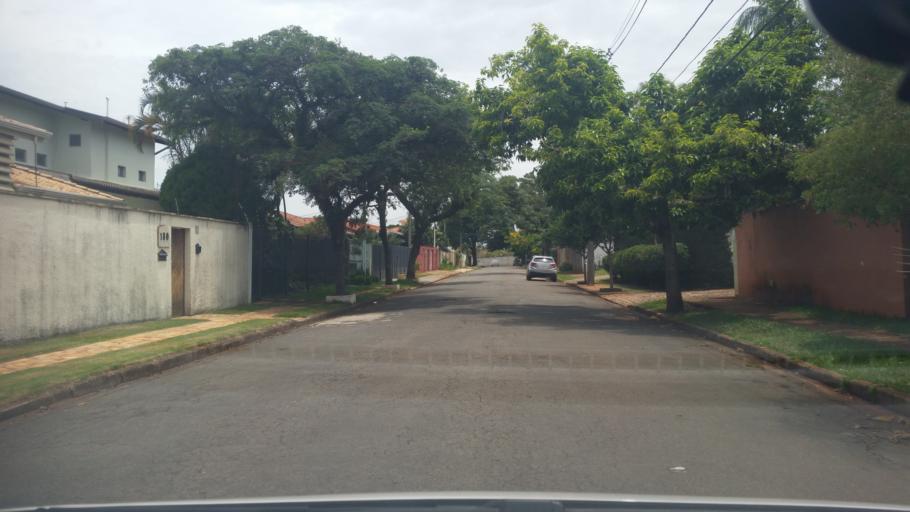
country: BR
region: Sao Paulo
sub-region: Campinas
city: Campinas
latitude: -22.8622
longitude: -47.0504
